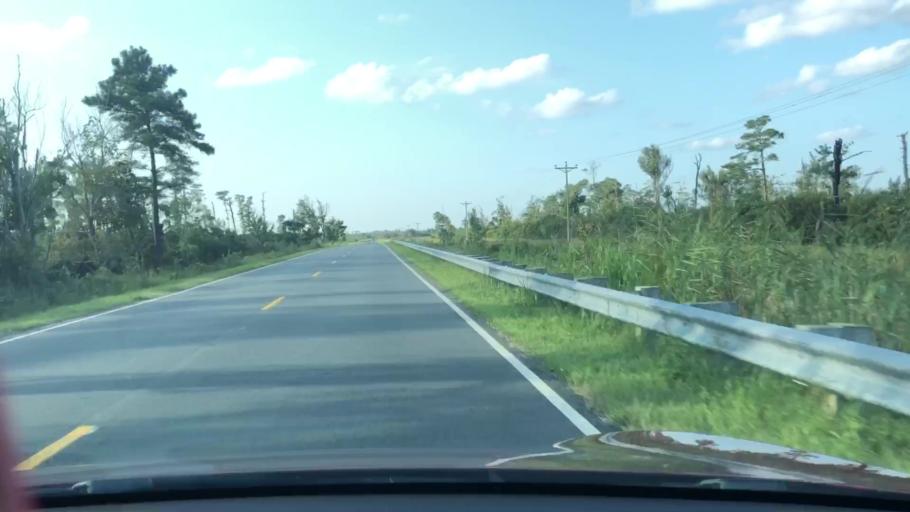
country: US
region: North Carolina
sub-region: Dare County
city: Wanchese
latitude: 35.6797
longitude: -75.7798
